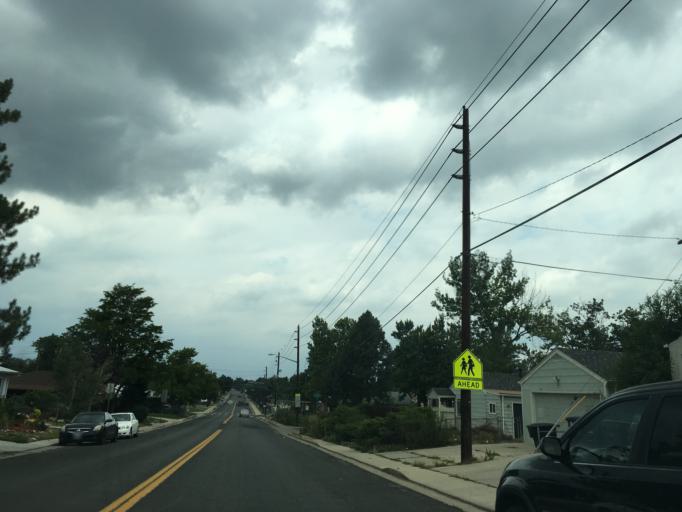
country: US
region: Colorado
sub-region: Arapahoe County
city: Sheridan
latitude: 39.6823
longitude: -105.0093
